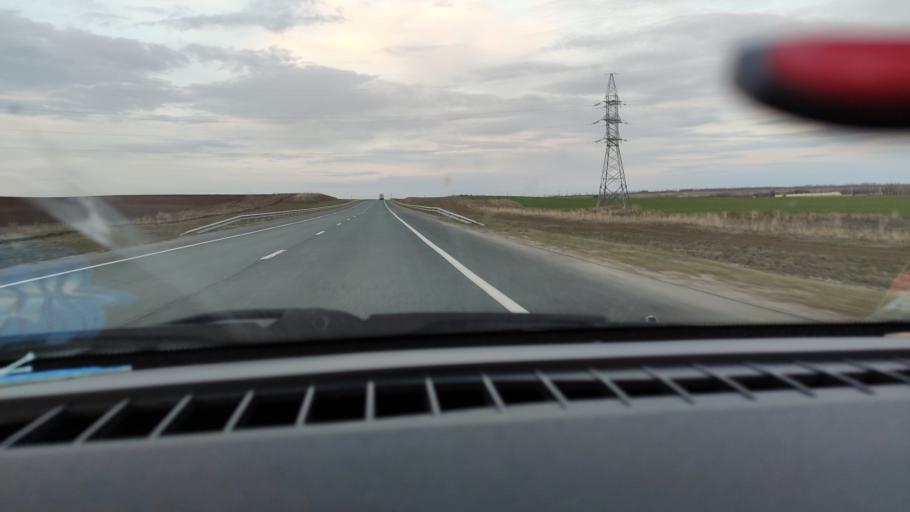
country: RU
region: Saratov
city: Yelshanka
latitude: 51.8292
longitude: 46.4048
